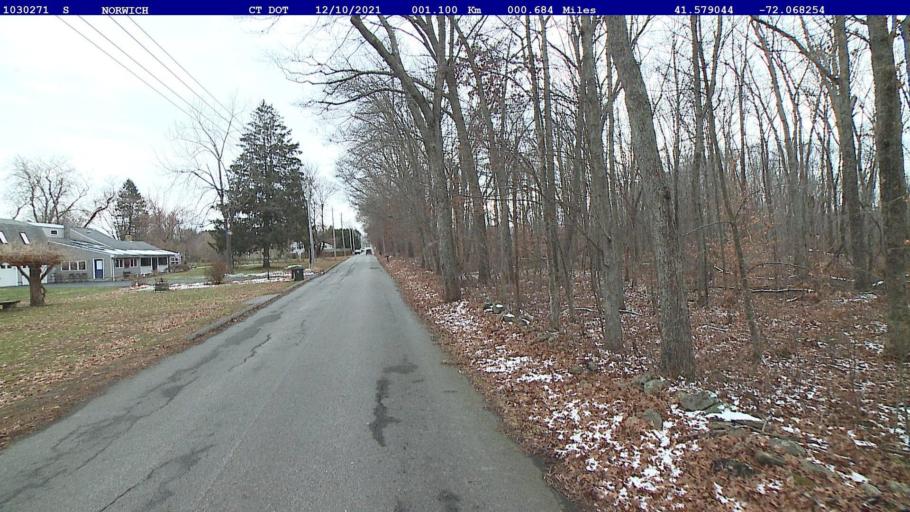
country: US
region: Connecticut
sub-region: New London County
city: Baltic
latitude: 41.5790
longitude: -72.0682
